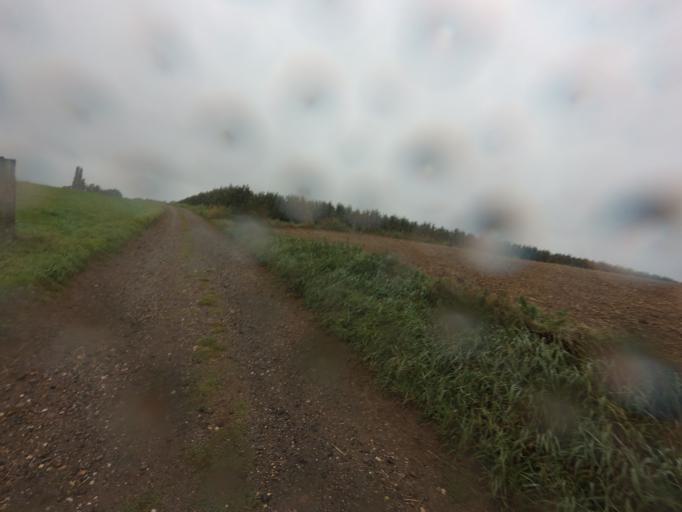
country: NL
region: Limburg
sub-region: Eijsden-Margraten
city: Margraten
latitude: 50.8005
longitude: 5.7811
